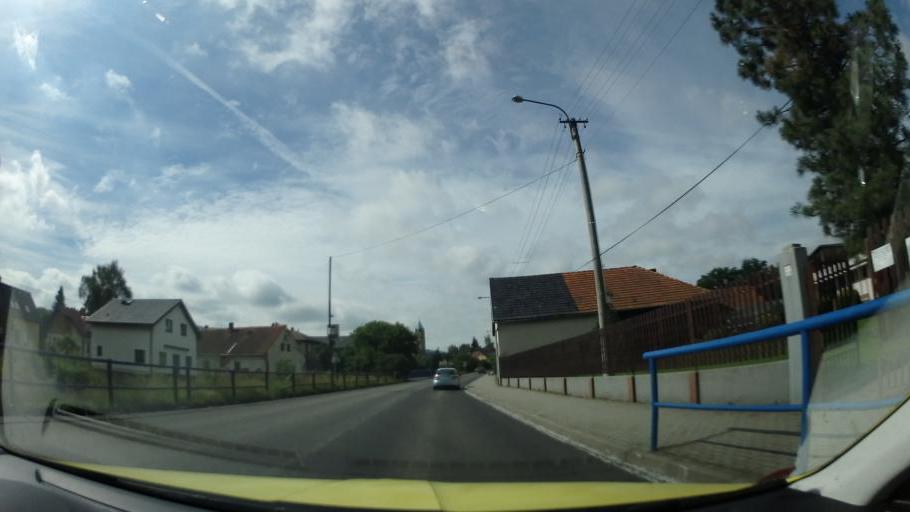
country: CZ
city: Hodslavice
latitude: 49.5413
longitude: 18.0256
